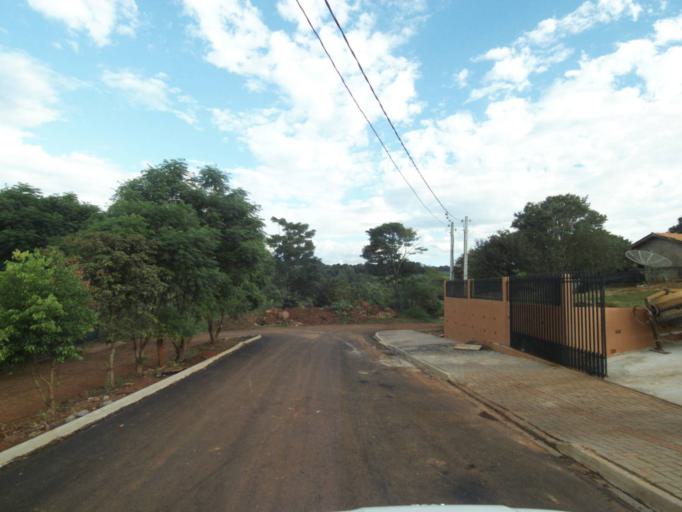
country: BR
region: Parana
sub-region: Laranjeiras Do Sul
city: Laranjeiras do Sul
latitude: -25.4927
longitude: -52.5236
